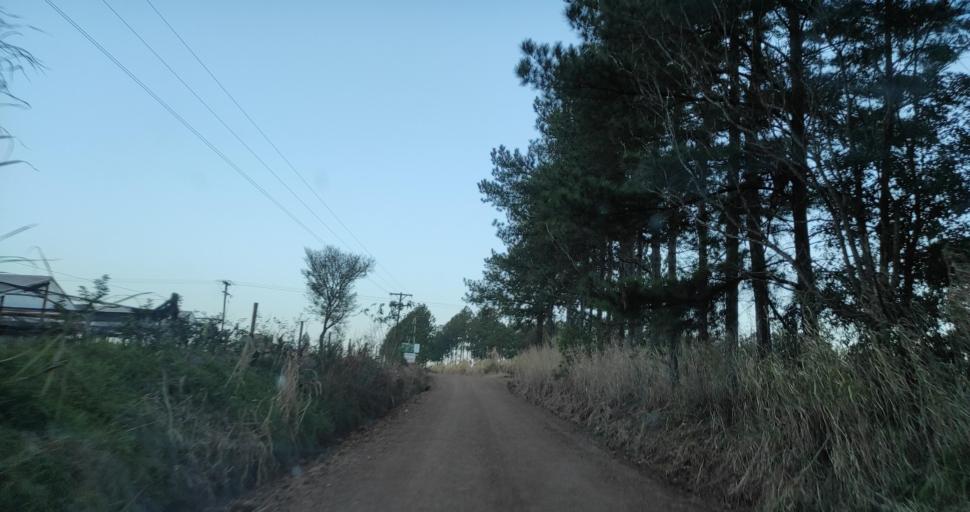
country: AR
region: Misiones
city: Capiovi
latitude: -26.8936
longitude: -55.0501
